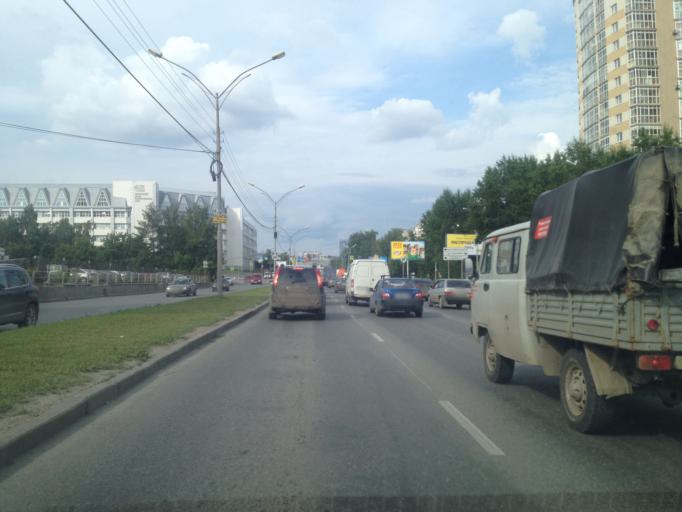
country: RU
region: Sverdlovsk
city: Sovkhoznyy
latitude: 56.8179
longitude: 60.5560
